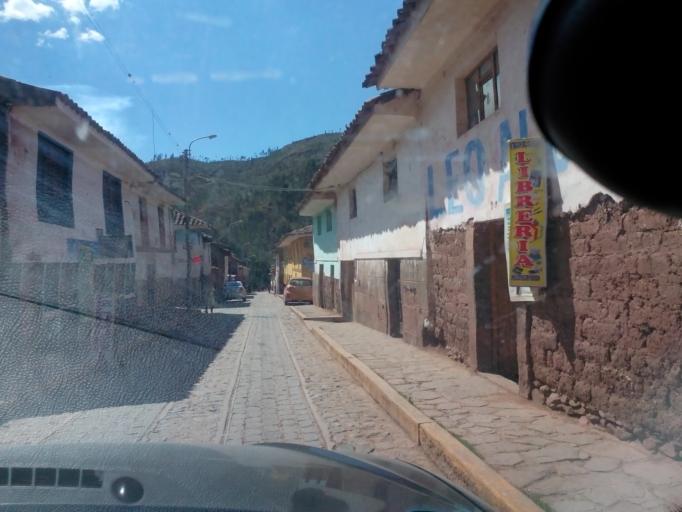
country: PE
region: Cusco
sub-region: Provincia de Anta
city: Huarocondo
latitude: -13.4137
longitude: -72.2074
